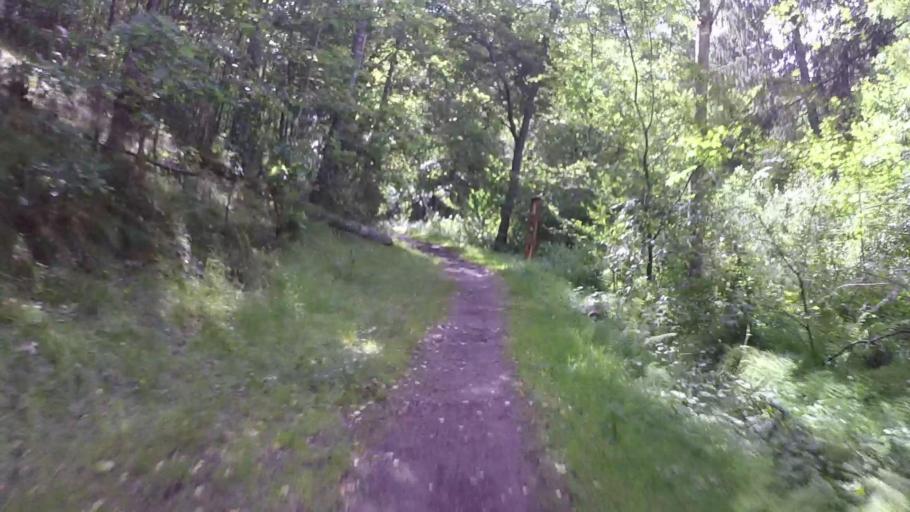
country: SE
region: Vaestra Goetaland
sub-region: Trollhattan
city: Trollhattan
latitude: 58.2523
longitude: 12.2682
